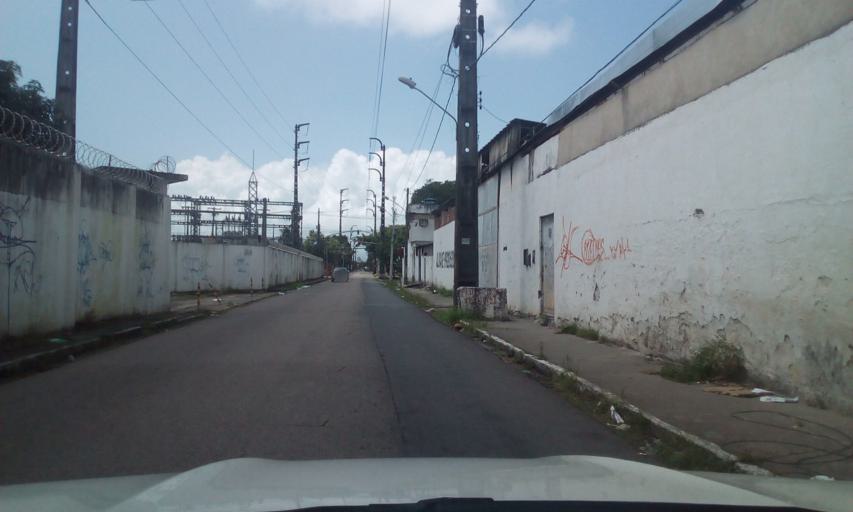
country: BR
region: Pernambuco
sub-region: Recife
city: Recife
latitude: -8.0648
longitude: -34.9282
